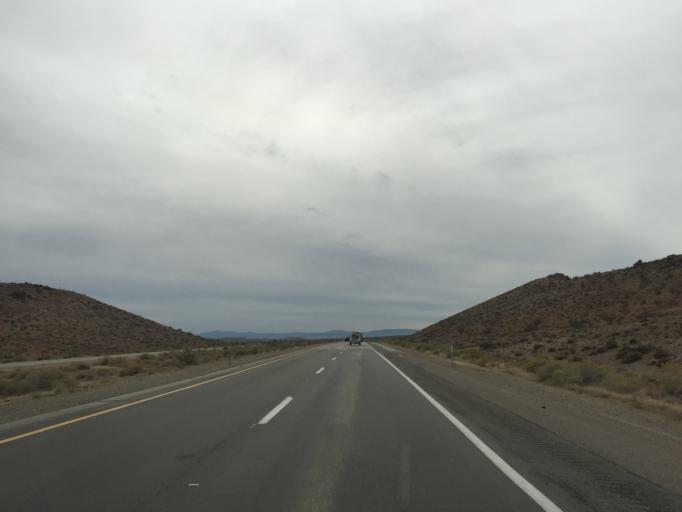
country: US
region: California
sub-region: Kern County
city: Mojave
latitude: 34.9748
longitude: -118.1596
